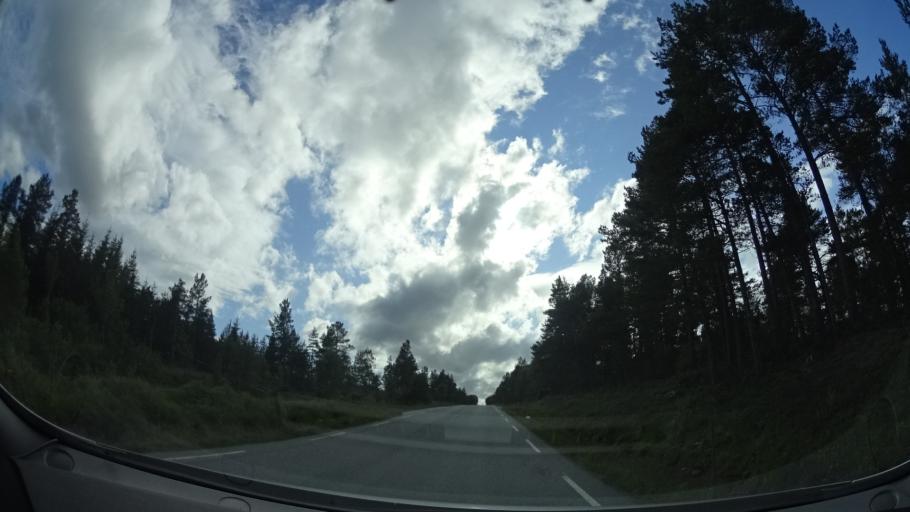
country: NO
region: More og Romsdal
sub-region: Halsa
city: Liaboen
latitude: 63.1255
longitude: 8.3558
